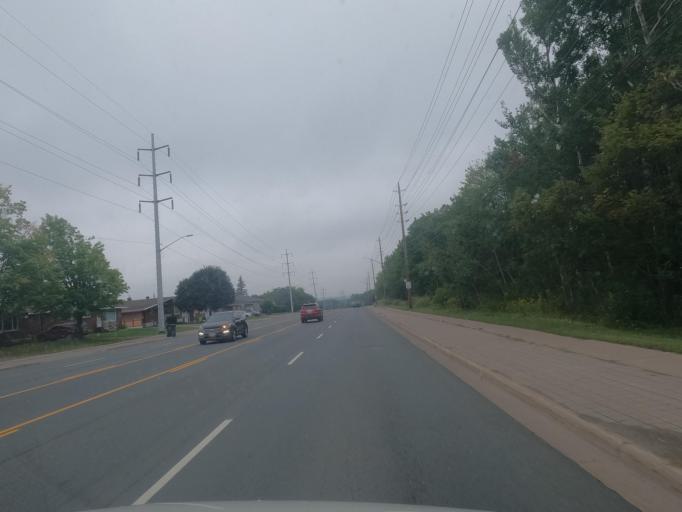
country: CA
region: Ontario
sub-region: Algoma
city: Sault Ste. Marie
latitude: 46.5386
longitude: -84.3360
